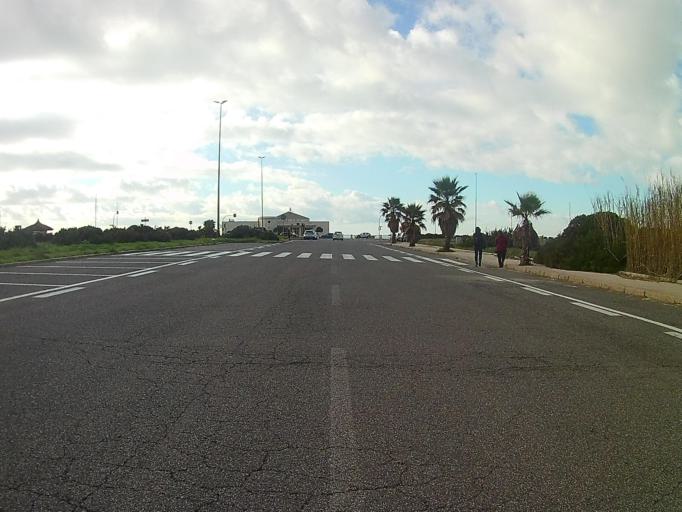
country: IT
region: Latium
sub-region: Citta metropolitana di Roma Capitale
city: Lido di Ostia
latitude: 41.7191
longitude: 12.3073
